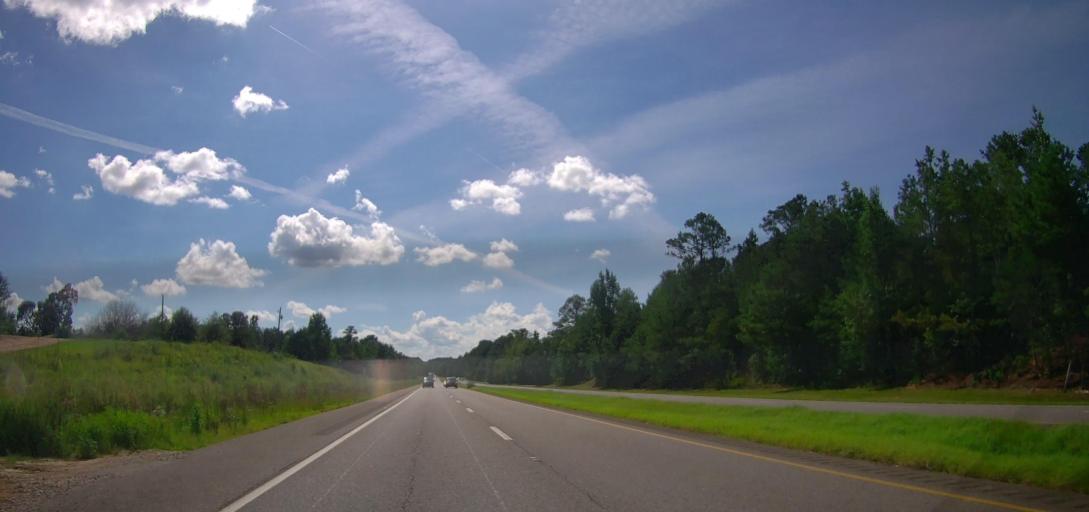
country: US
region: Alabama
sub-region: Pickens County
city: Gordo
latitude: 33.2833
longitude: -87.8279
